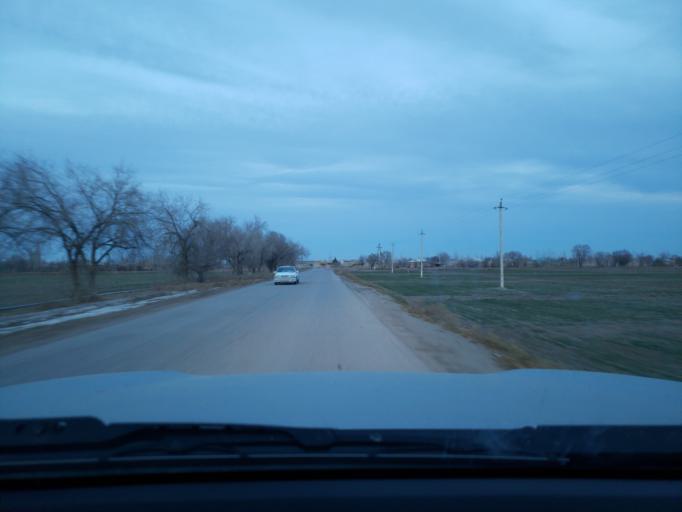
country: TM
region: Dasoguz
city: Tagta
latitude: 41.6281
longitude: 60.0653
